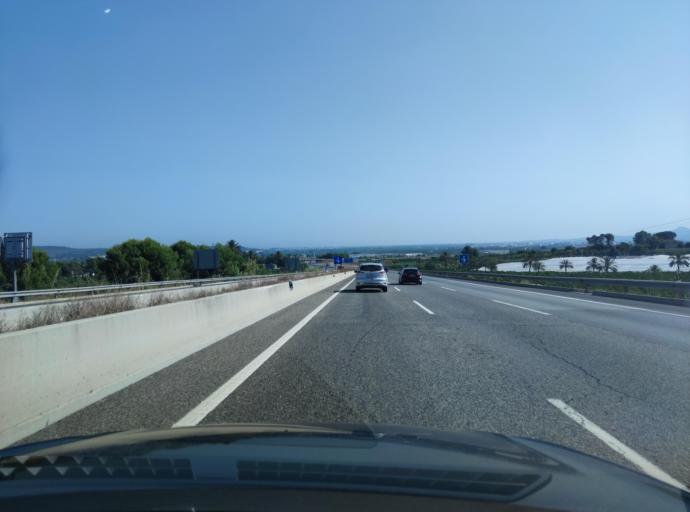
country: ES
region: Valencia
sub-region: Provincia de Valencia
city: Beneixida
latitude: 39.0510
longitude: -0.5470
